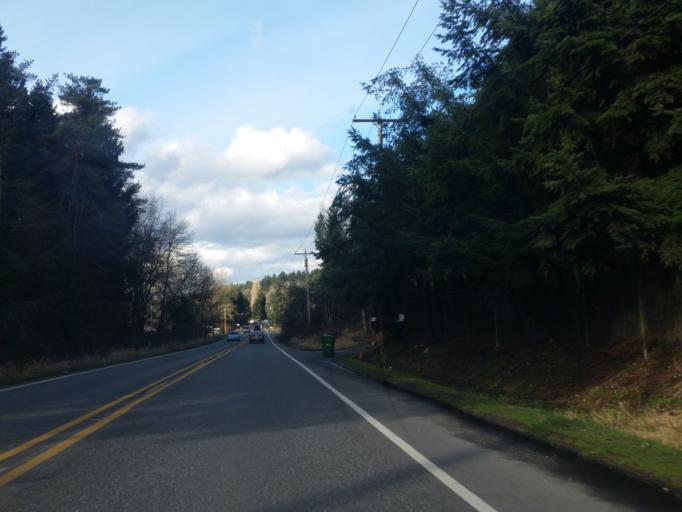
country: US
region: Washington
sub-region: King County
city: Woodinville
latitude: 47.7204
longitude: -122.1349
